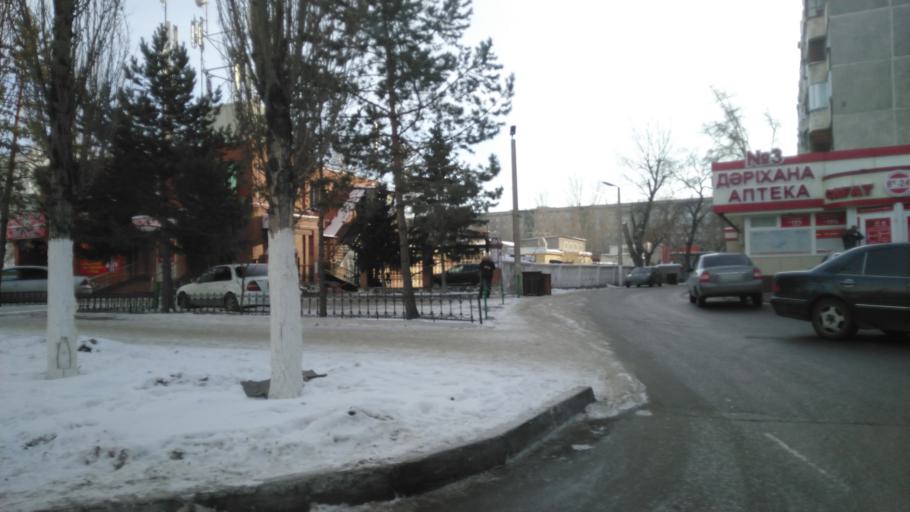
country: KZ
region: Pavlodar
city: Pavlodar
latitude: 52.2675
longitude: 76.9470
